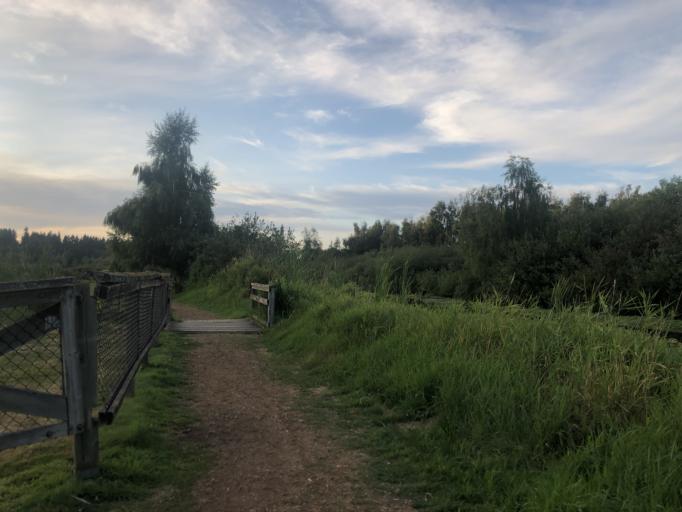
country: US
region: Washington
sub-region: King County
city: Newport
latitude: 47.5894
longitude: -122.1873
